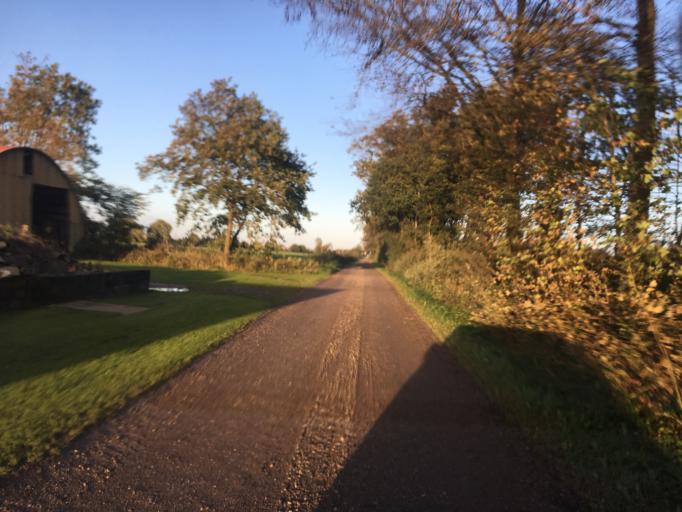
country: DE
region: Schleswig-Holstein
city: Ellhoft
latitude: 54.9400
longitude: 9.0128
